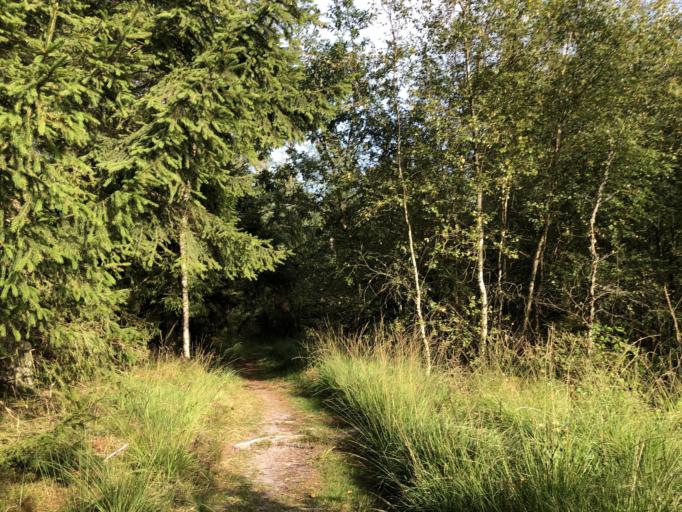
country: DK
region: Central Jutland
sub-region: Lemvig Kommune
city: Lemvig
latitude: 56.4690
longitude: 8.3278
